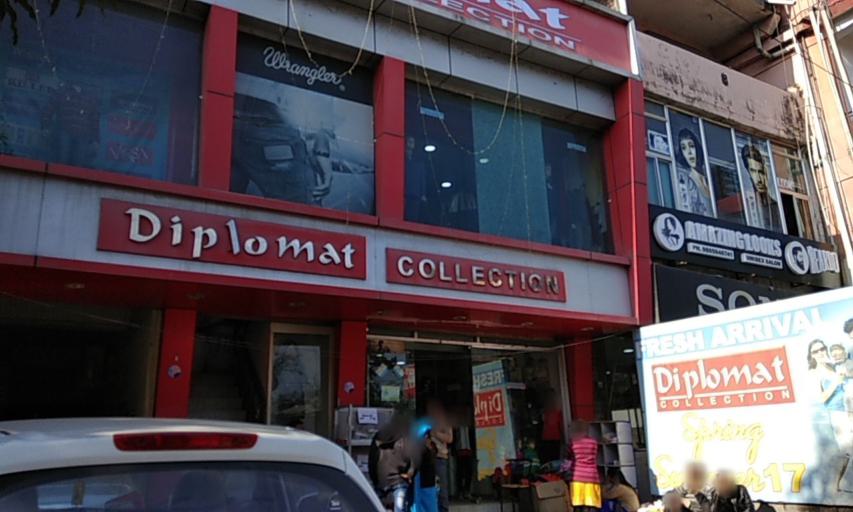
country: IN
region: Himachal Pradesh
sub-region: Kangra
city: Kangra
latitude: 32.1094
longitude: 76.2774
